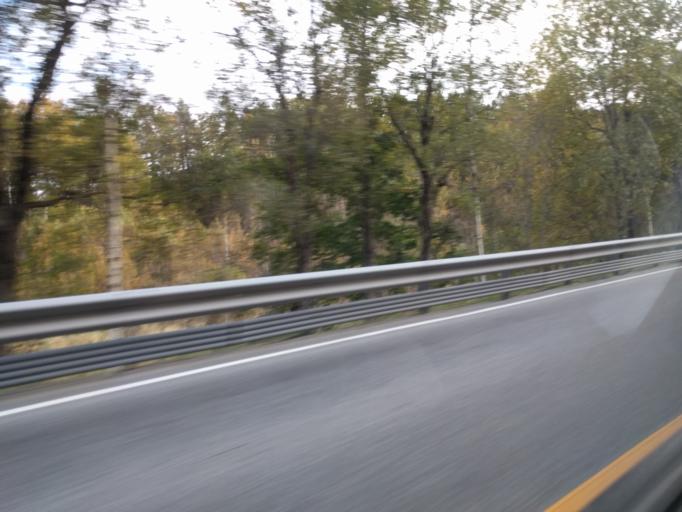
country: NO
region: Vest-Agder
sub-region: Kristiansand
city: Strai
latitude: 58.2539
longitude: 7.8561
